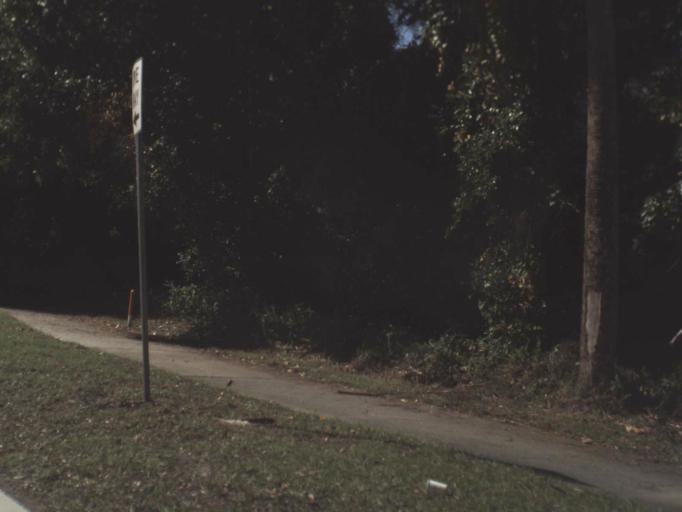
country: US
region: Florida
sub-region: Flagler County
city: Palm Coast
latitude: 29.5641
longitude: -81.1930
